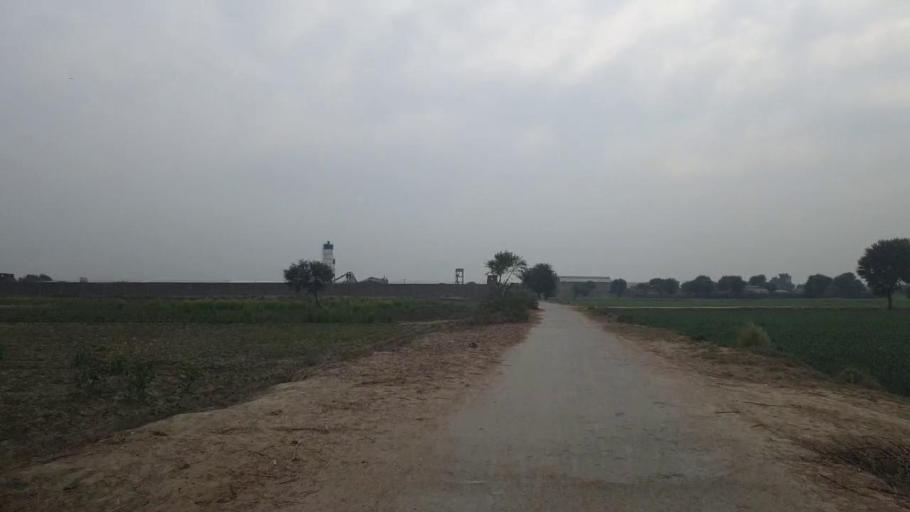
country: PK
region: Sindh
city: Shahdadpur
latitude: 25.9387
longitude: 68.7013
